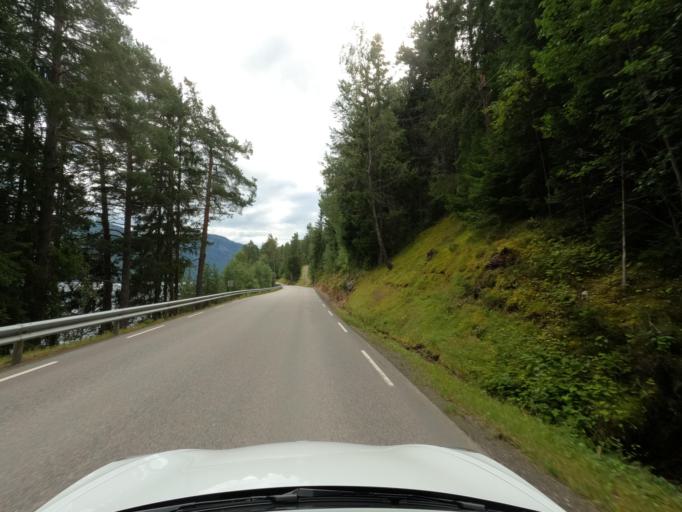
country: NO
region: Telemark
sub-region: Tinn
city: Rjukan
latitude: 59.9701
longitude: 8.8030
